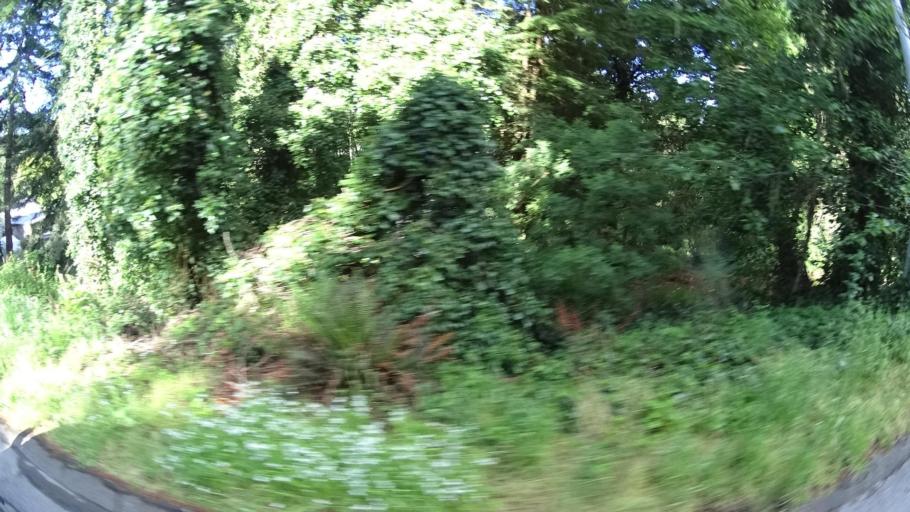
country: US
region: California
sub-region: Humboldt County
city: Westhaven-Moonstone
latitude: 41.0330
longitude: -124.1095
